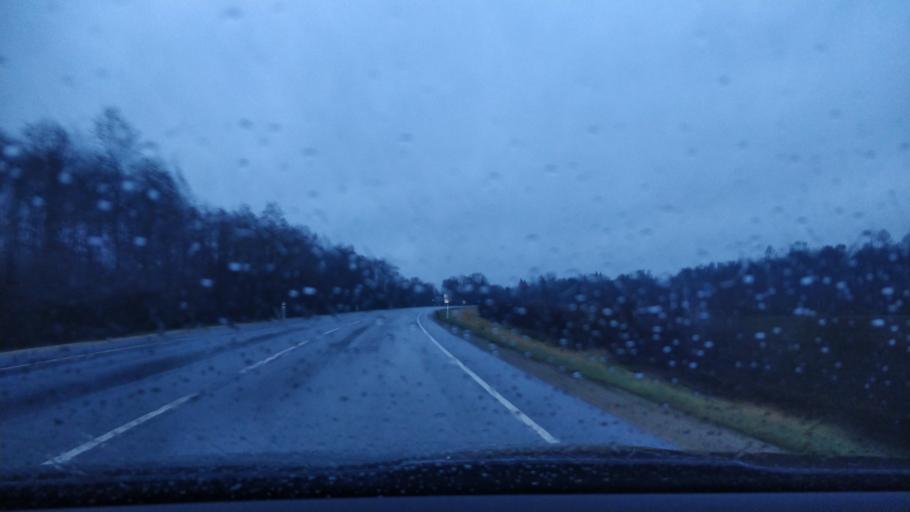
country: EE
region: Laeaene
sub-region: Lihula vald
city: Lihula
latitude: 58.8223
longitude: 24.0577
